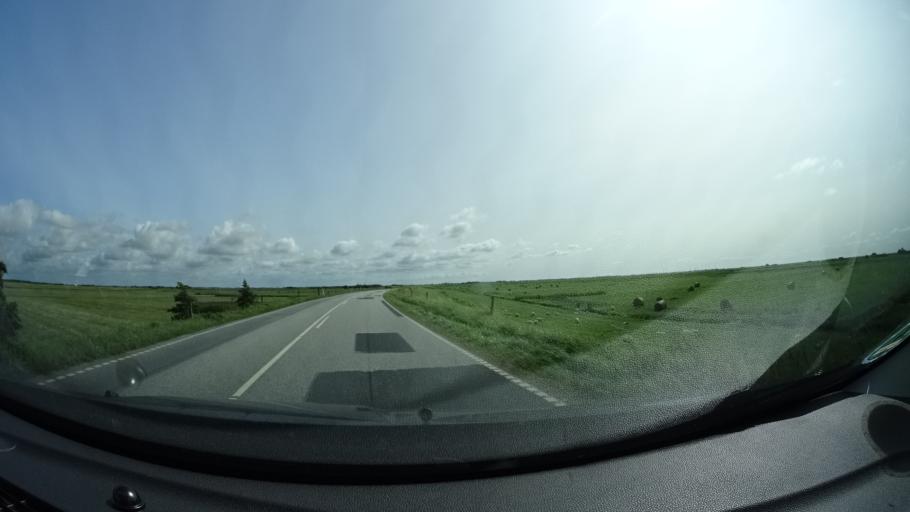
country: DE
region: Schleswig-Holstein
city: Rodenas
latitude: 54.9555
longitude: 8.7023
